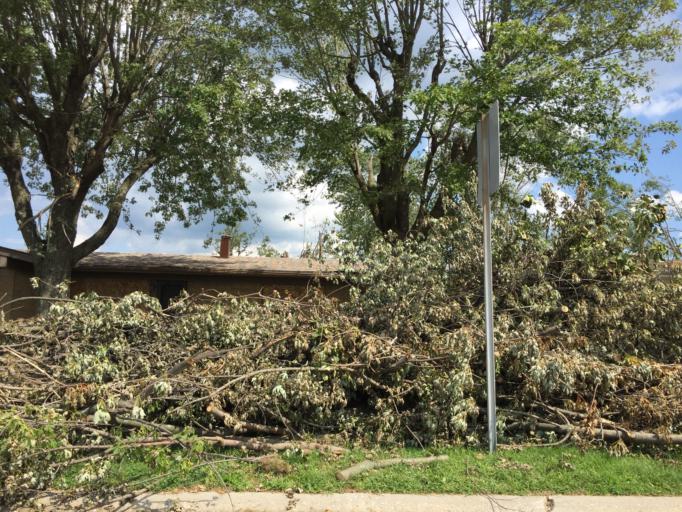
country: US
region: Indiana
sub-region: Howard County
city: Kokomo
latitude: 40.4694
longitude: -86.1075
